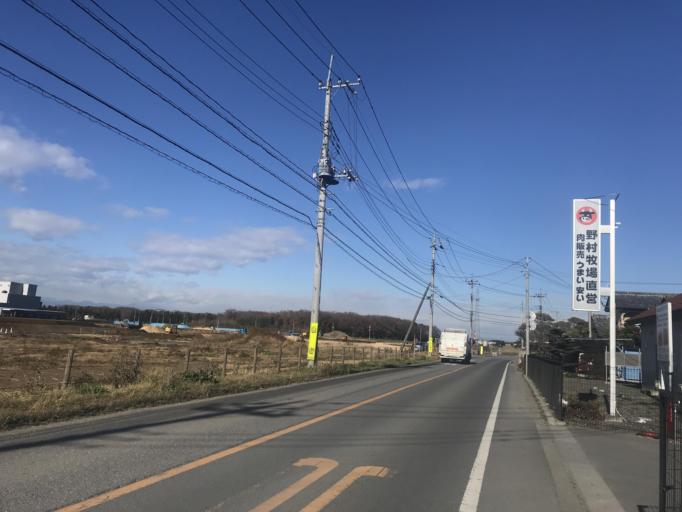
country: JP
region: Ibaraki
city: Yuki
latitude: 36.3620
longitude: 139.8767
